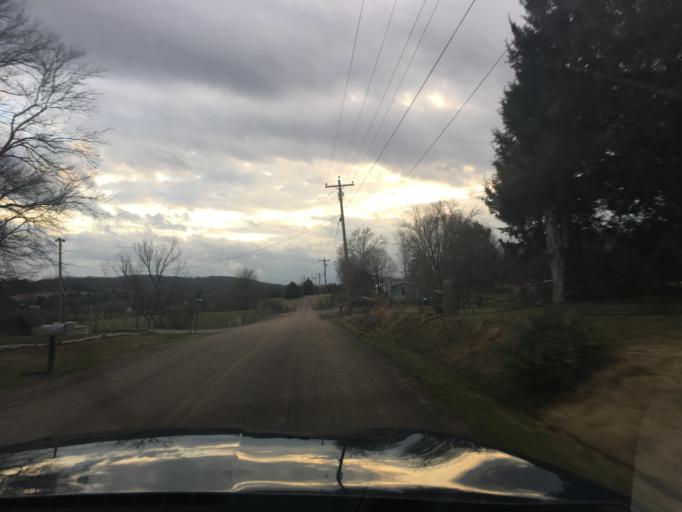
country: US
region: Tennessee
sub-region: Meigs County
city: Decatur
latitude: 35.5981
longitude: -84.6752
